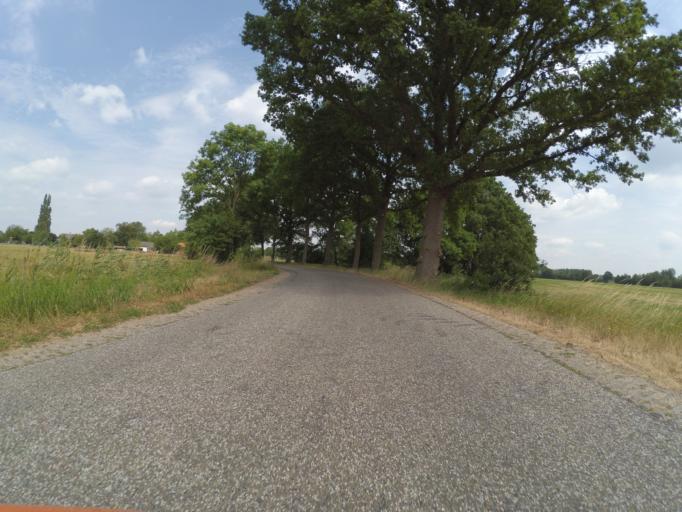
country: NL
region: Overijssel
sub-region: Gemeente Hof van Twente
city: Diepenheim
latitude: 52.1741
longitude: 6.5185
